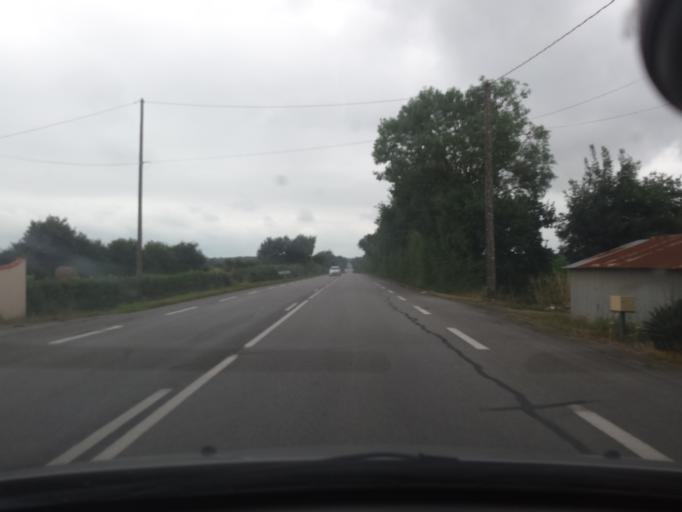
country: FR
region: Pays de la Loire
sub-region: Departement de la Vendee
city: Saint-Florent-des-Bois
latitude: 46.5823
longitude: -1.2983
